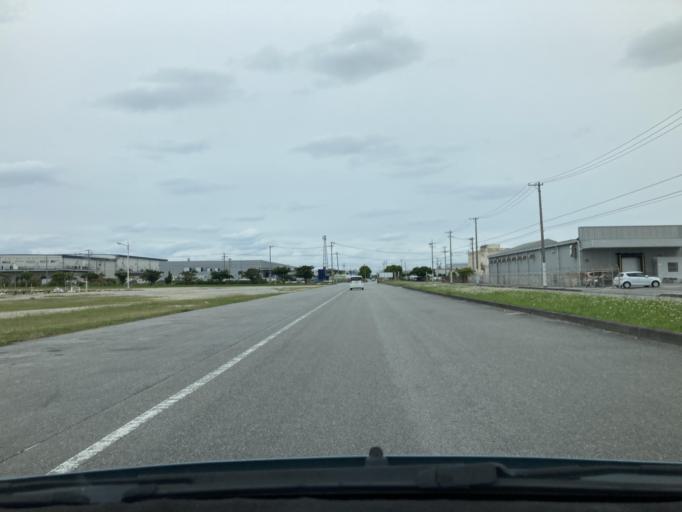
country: JP
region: Okinawa
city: Itoman
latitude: 26.1357
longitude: 127.6613
